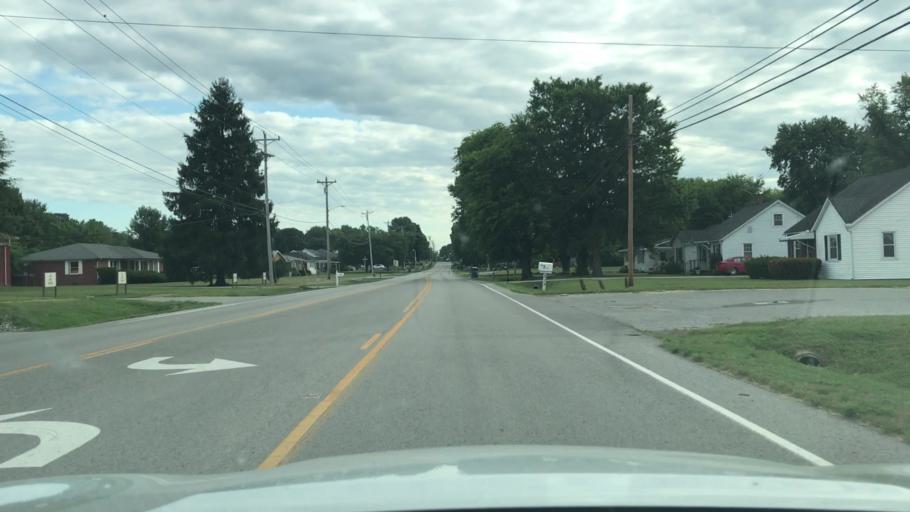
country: US
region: Kentucky
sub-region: Todd County
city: Elkton
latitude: 36.7978
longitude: -87.1596
